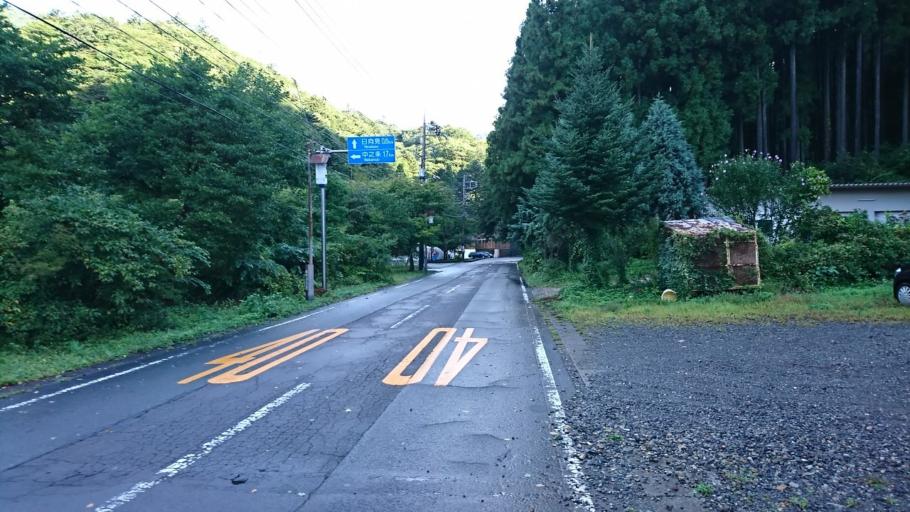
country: JP
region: Gunma
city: Nakanojomachi
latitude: 36.6916
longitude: 138.7745
